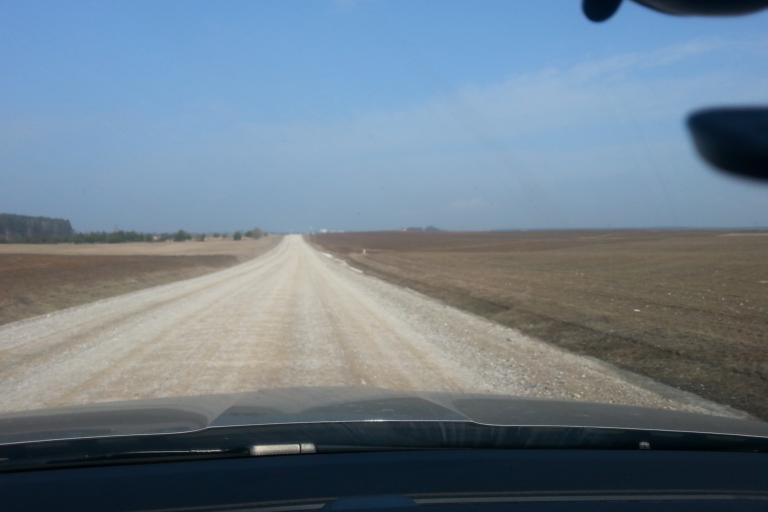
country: LT
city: Trakai
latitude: 54.5882
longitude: 24.9770
